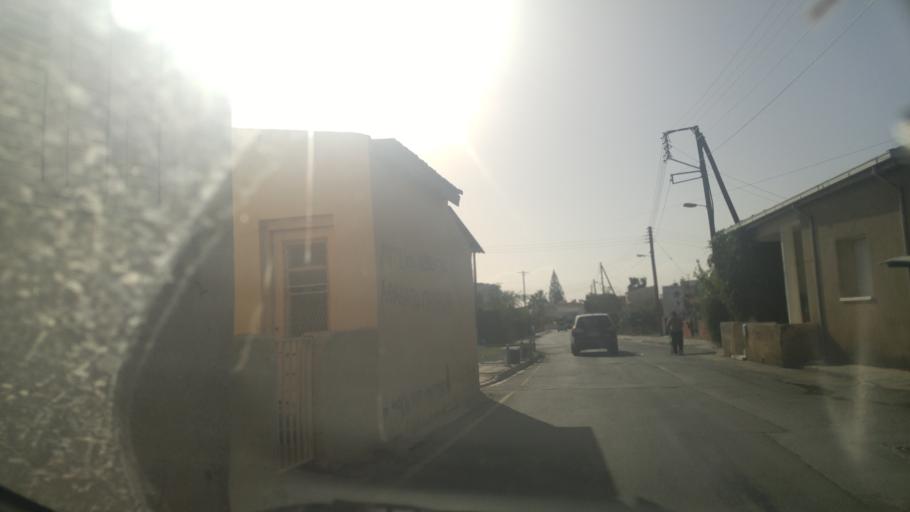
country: CY
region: Limassol
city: Pano Polemidia
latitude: 34.6924
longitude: 32.9955
